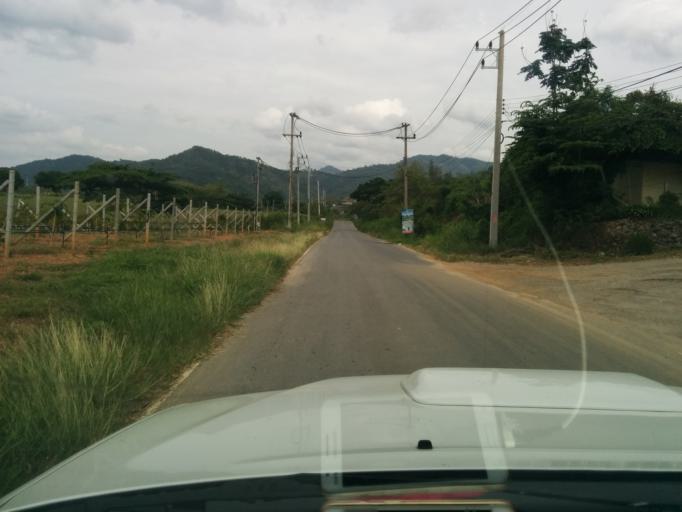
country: TH
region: Sara Buri
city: Muak Lek
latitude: 14.5638
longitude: 101.2502
